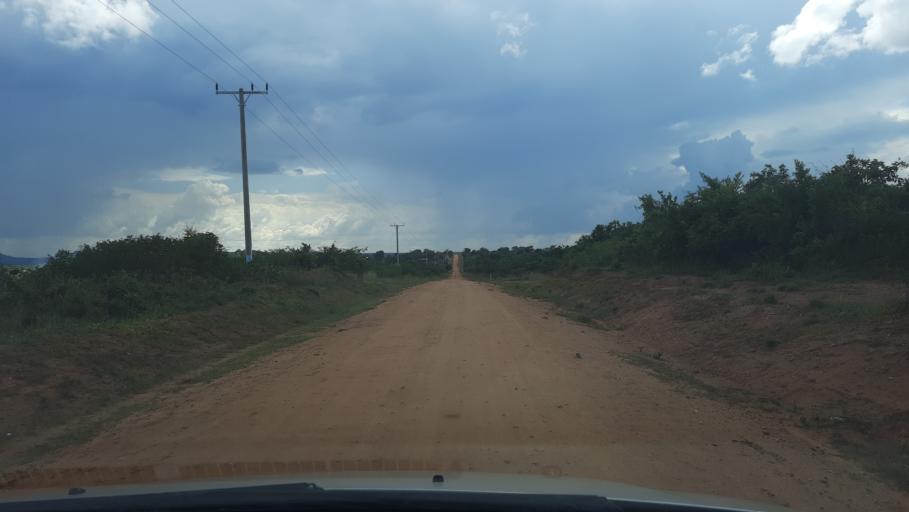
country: UG
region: Central Region
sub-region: Nakasongola District
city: Nakasongola
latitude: 1.3811
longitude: 32.5098
